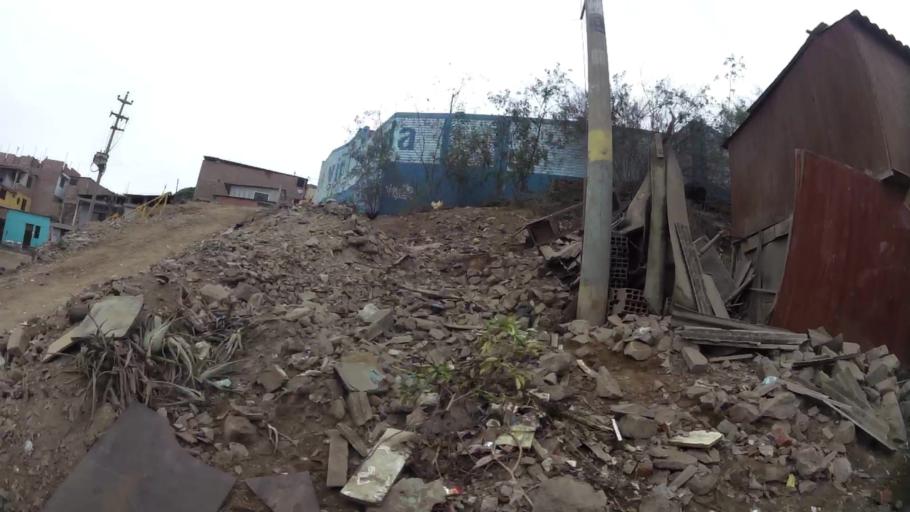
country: PE
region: Lima
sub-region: Lima
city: Surco
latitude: -12.1673
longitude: -76.9568
